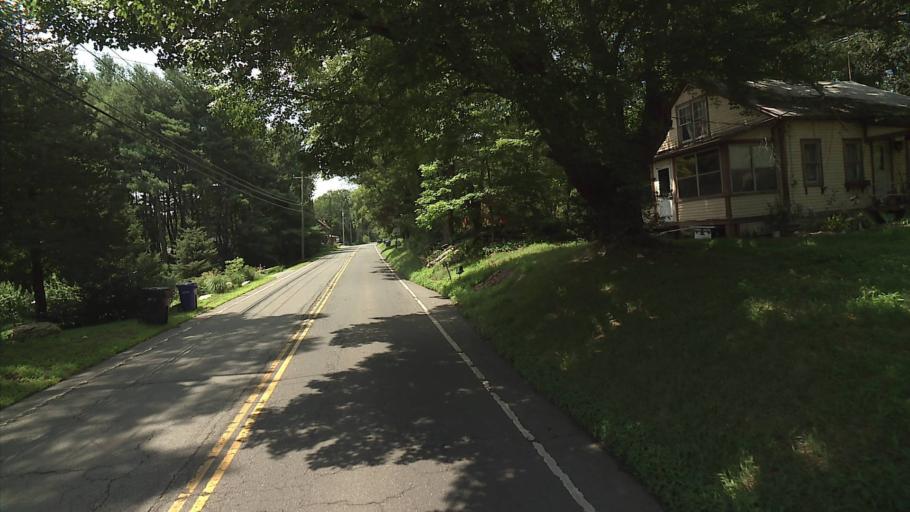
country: US
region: Connecticut
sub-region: Tolland County
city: South Coventry
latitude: 41.7620
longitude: -72.2807
